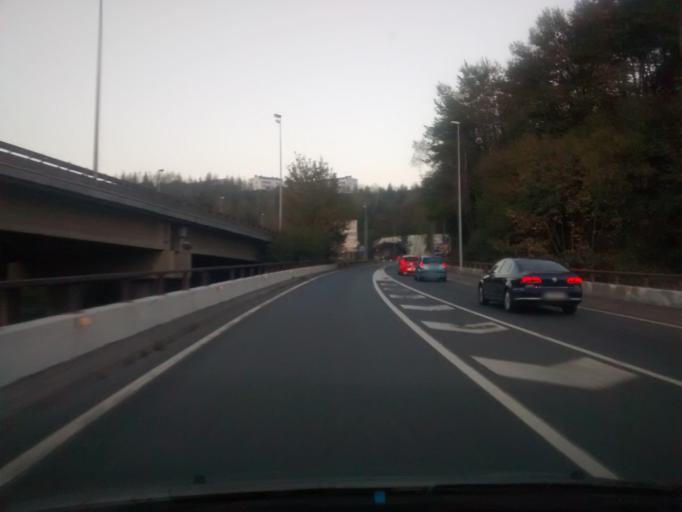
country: ES
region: Basque Country
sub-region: Provincia de Guipuzcoa
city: San Sebastian
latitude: 43.2957
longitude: -1.9960
